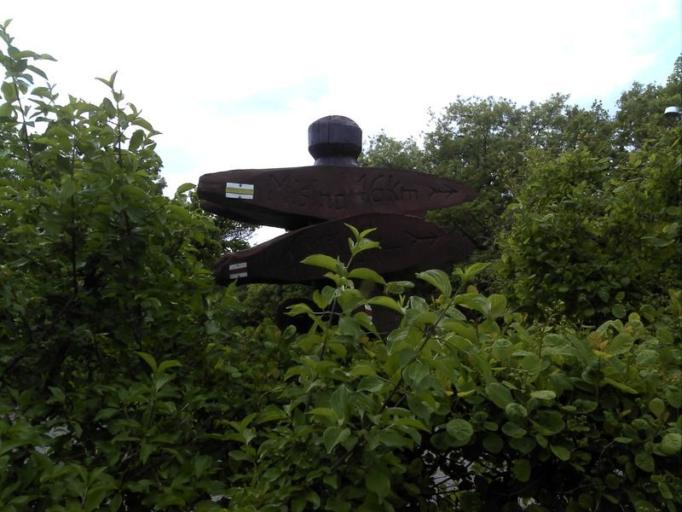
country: HU
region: Baranya
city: Pecs
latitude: 46.0996
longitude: 18.2311
